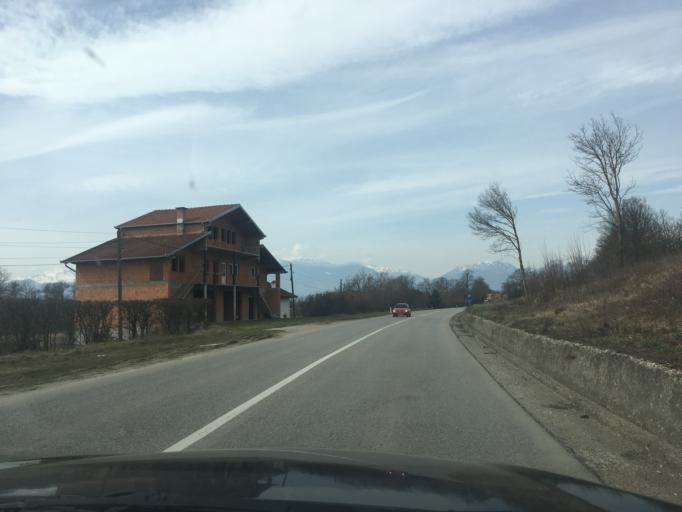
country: XK
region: Pec
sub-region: Komuna e Pejes
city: Kosuriq
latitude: 42.6206
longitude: 20.4793
